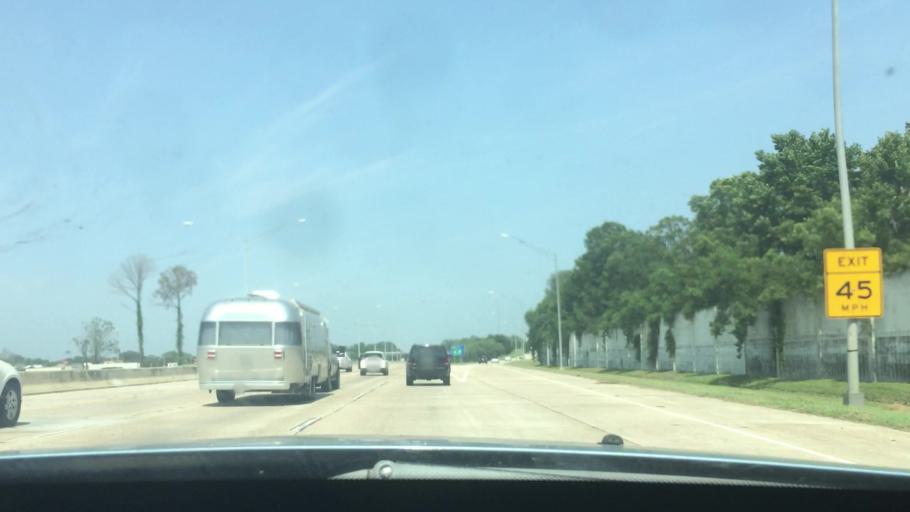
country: US
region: Louisiana
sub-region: East Baton Rouge Parish
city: Shenandoah
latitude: 30.4365
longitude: -91.0306
